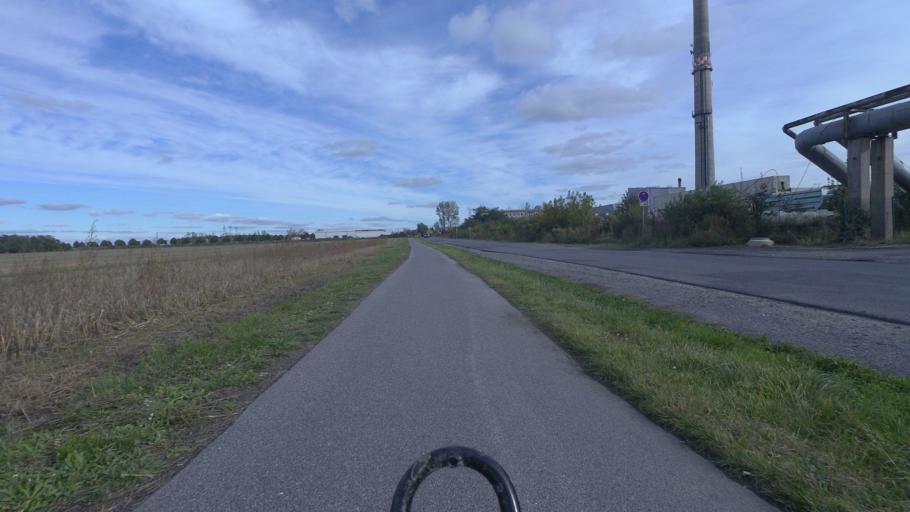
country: DE
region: Brandenburg
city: Ludwigsfelde
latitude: 52.3148
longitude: 13.2773
